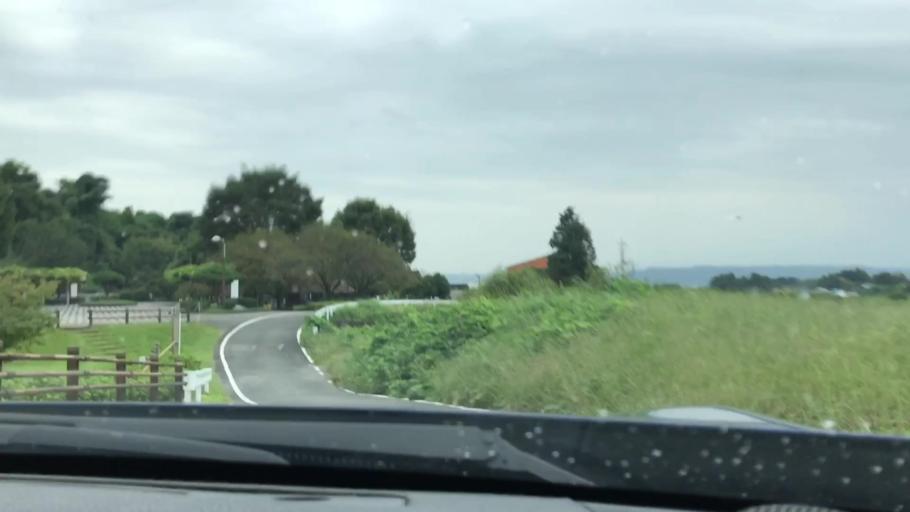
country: JP
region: Gunma
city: Kanekomachi
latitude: 36.3955
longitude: 138.9510
